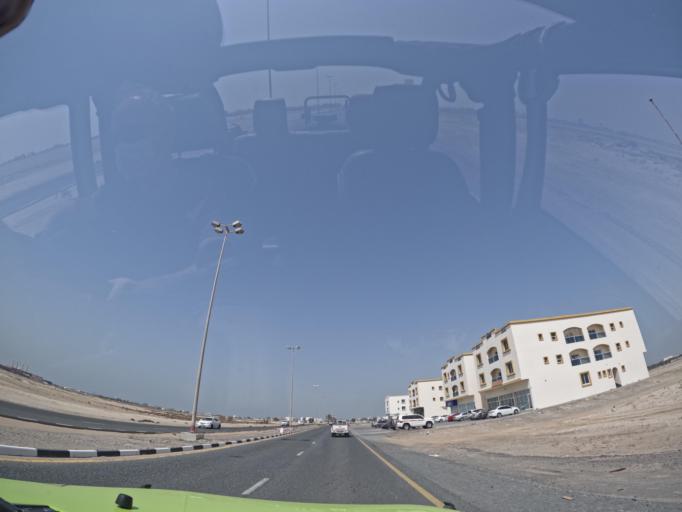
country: AE
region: Umm al Qaywayn
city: Umm al Qaywayn
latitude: 25.5194
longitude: 55.5547
